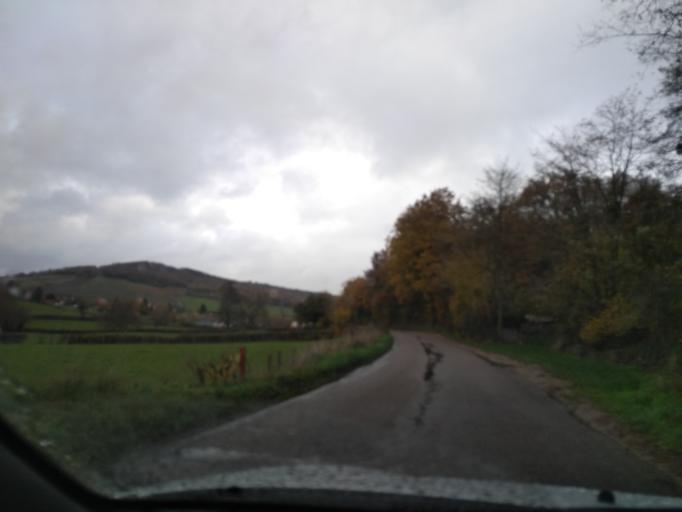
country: FR
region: Bourgogne
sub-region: Departement de Saone-et-Loire
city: Saint-Leger-sur-Dheune
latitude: 46.8614
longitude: 4.6867
